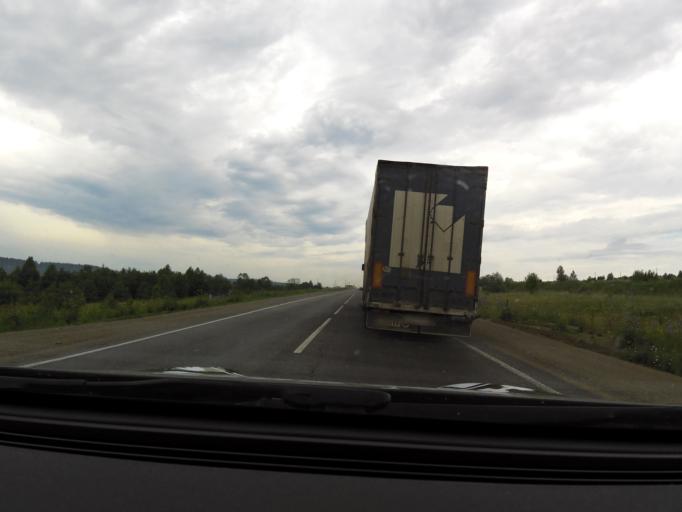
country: RU
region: Chelyabinsk
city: Sim
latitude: 55.0042
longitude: 57.6707
